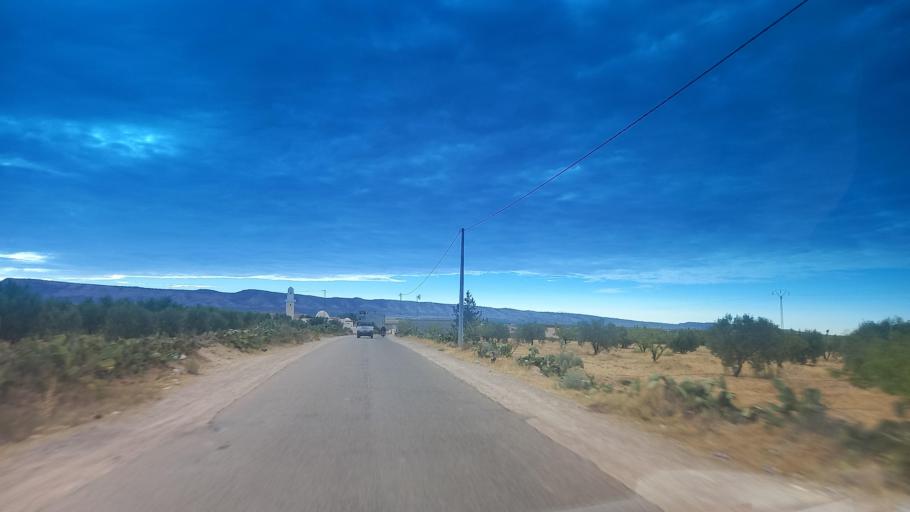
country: TN
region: Al Qasrayn
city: Sbiba
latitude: 35.3643
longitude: 9.0870
